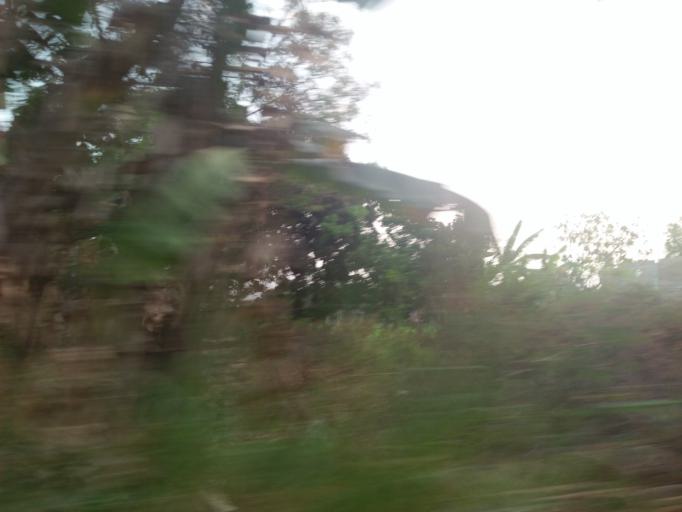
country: ID
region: Daerah Istimewa Yogyakarta
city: Sewon
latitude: -7.8457
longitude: 110.4034
